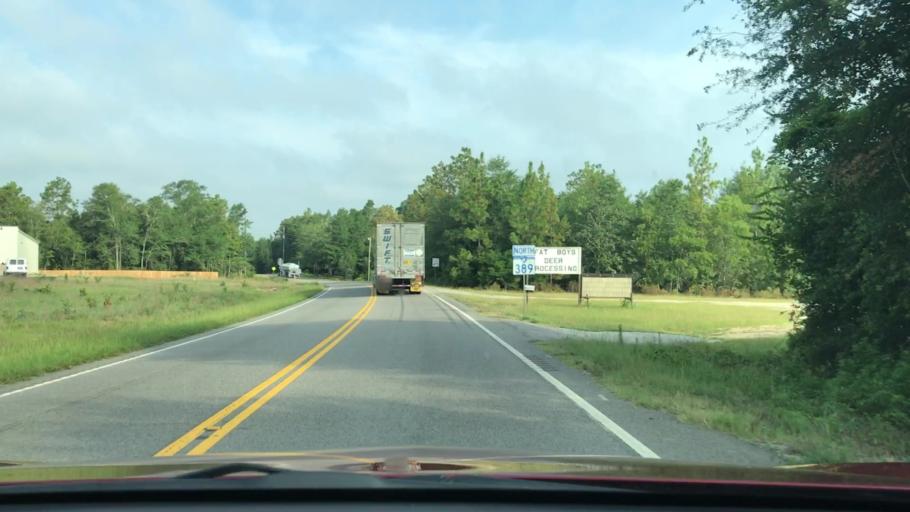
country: US
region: South Carolina
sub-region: Barnwell County
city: Williston
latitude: 33.6293
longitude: -81.3030
